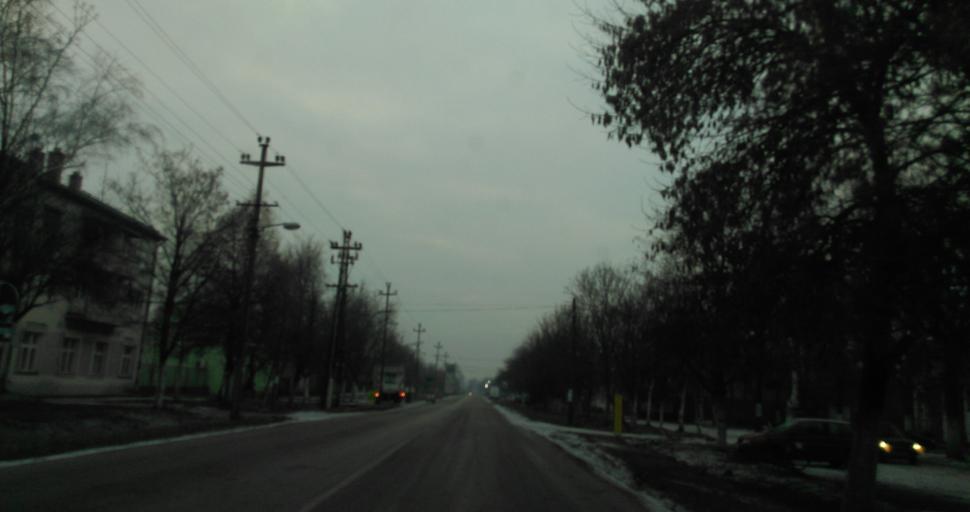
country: RS
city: Kumane
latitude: 45.5368
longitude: 20.2284
